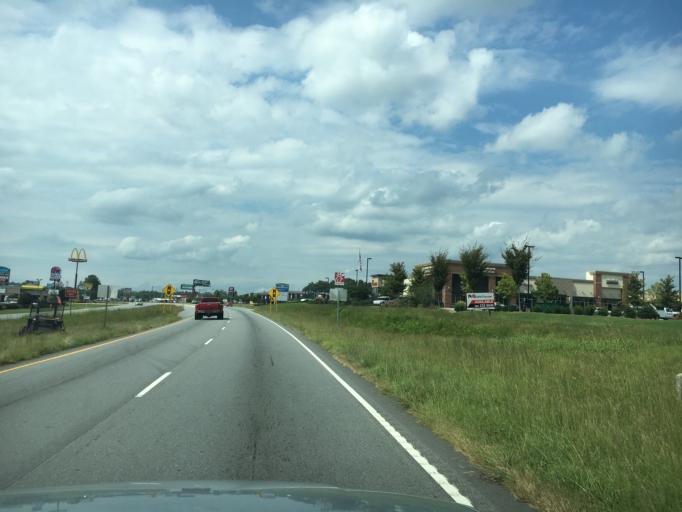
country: US
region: South Carolina
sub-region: Anderson County
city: Powdersville
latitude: 34.7864
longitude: -82.4781
